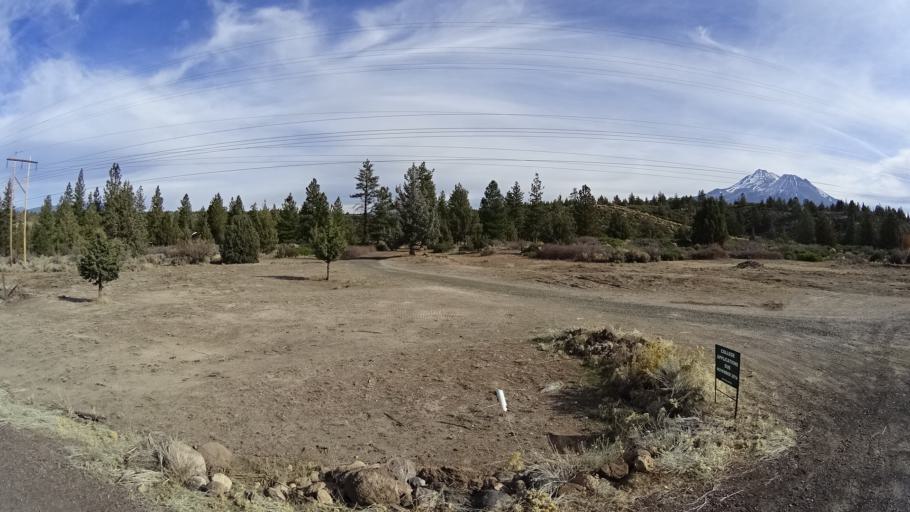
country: US
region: California
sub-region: Siskiyou County
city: Weed
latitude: 41.5034
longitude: -122.3635
